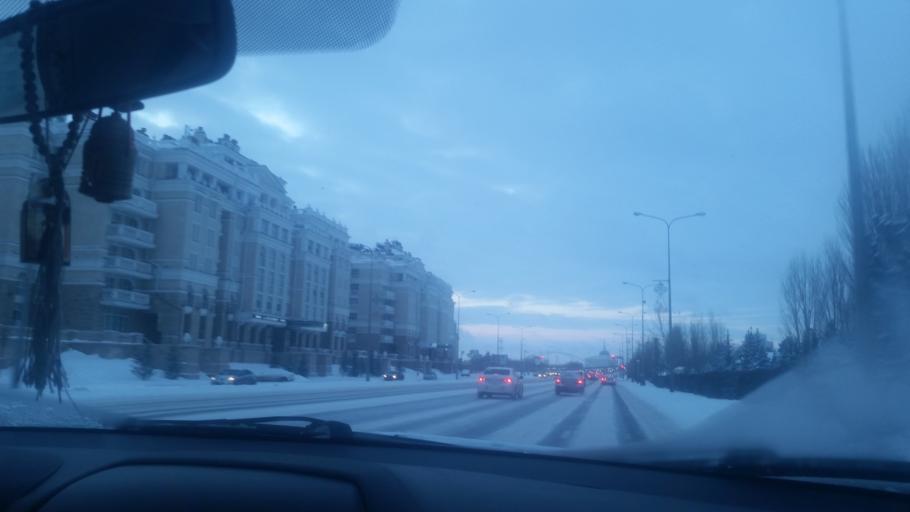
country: KZ
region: Astana Qalasy
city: Astana
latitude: 51.1441
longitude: 71.4449
